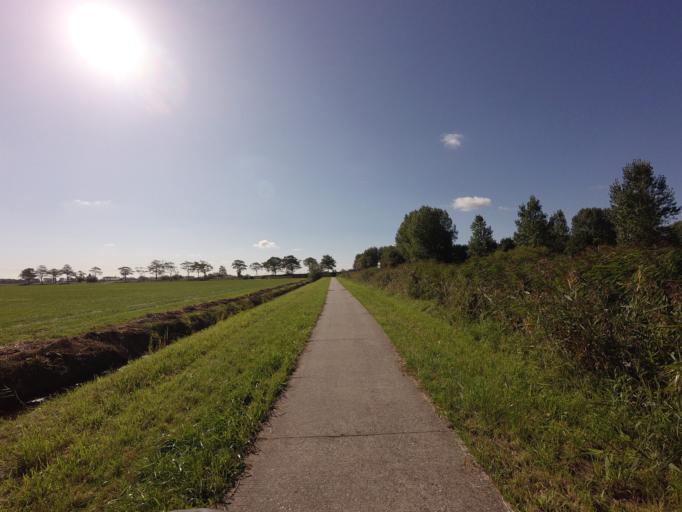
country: NL
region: Friesland
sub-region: Gemeente Leeuwarden
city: Wirdum
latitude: 53.1503
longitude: 5.7638
